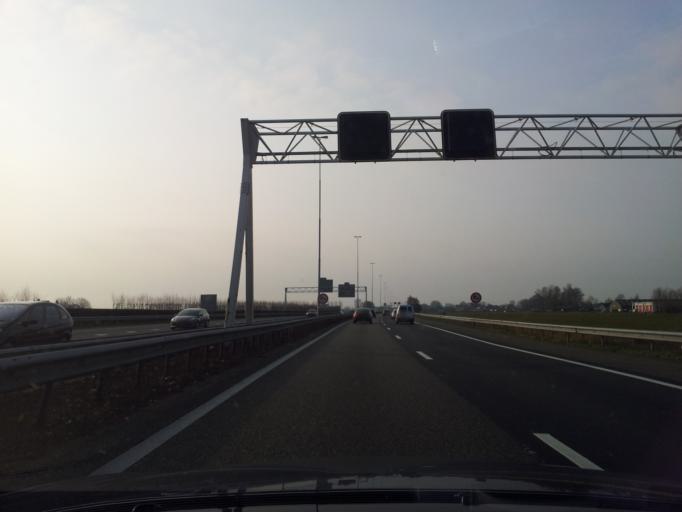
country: NL
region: North Brabant
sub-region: Gemeente Woudrichem
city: Almkerk
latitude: 51.7673
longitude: 4.9280
